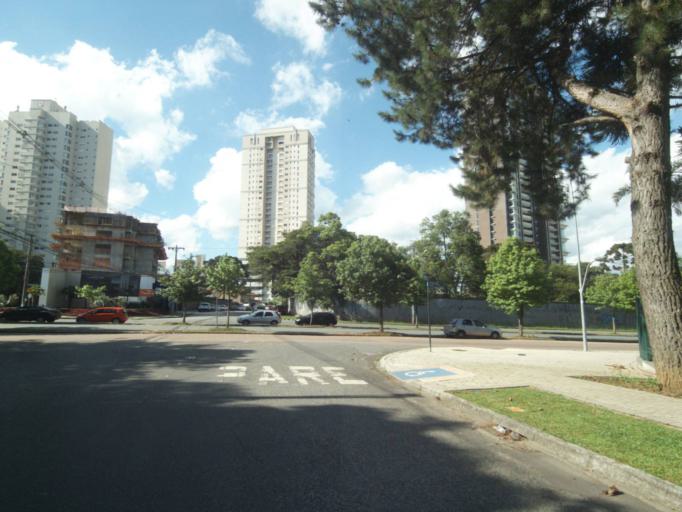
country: BR
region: Parana
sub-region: Curitiba
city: Curitiba
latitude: -25.4414
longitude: -49.3432
